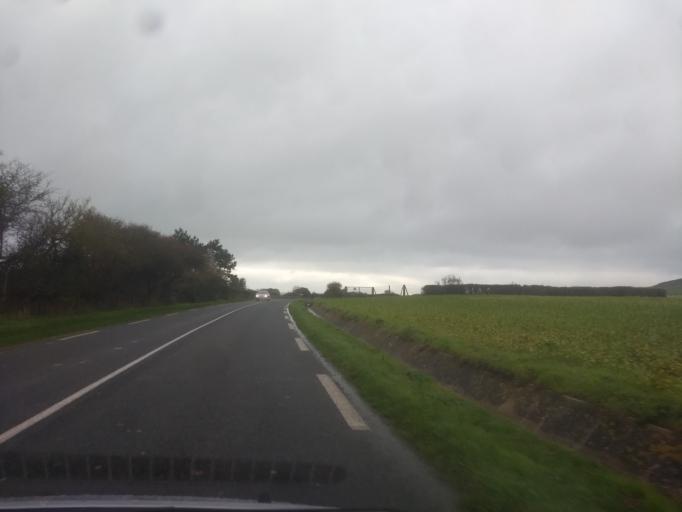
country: FR
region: Nord-Pas-de-Calais
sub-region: Departement du Pas-de-Calais
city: Wissant
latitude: 50.9002
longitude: 1.6833
